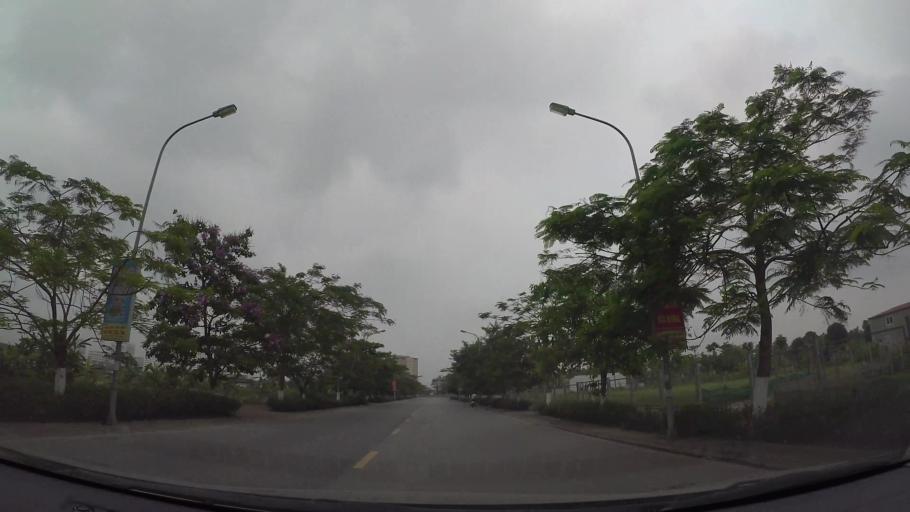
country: VN
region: Ha Noi
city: Trau Quy
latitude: 21.0535
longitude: 105.9199
